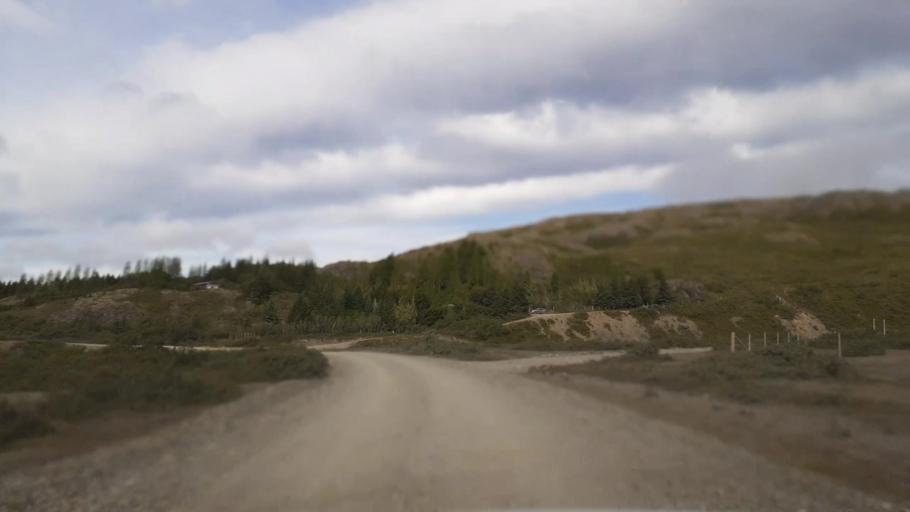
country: IS
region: East
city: Hoefn
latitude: 64.4359
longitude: -14.9010
